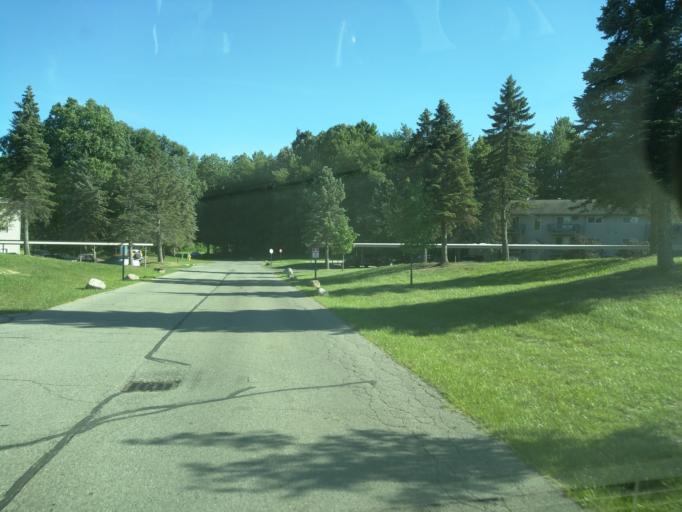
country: US
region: Michigan
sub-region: Eaton County
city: Waverly
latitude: 42.7366
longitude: -84.6386
